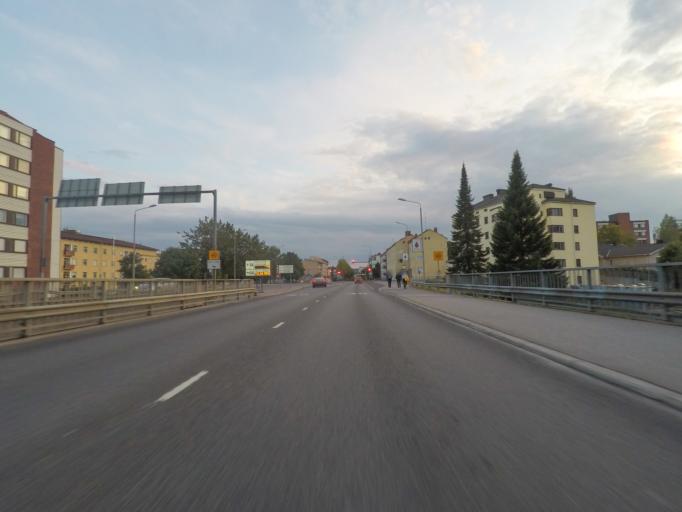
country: FI
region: Central Finland
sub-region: Jyvaeskylae
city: Jyvaeskylae
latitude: 62.2468
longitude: 25.7598
